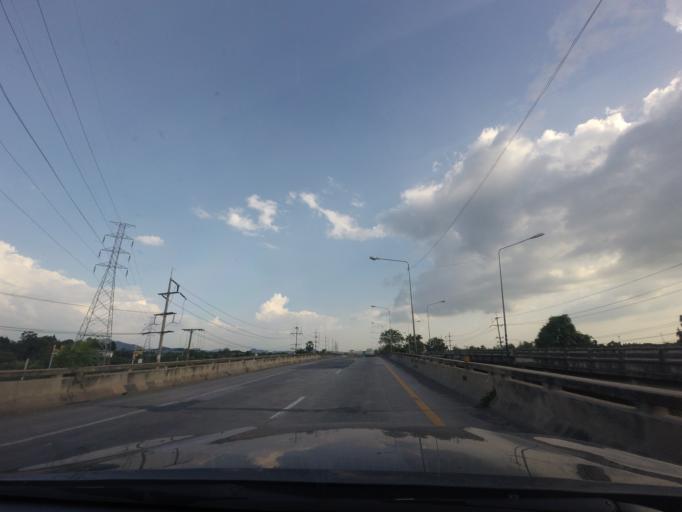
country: TH
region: Sara Buri
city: Saraburi
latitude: 14.5253
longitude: 100.8882
